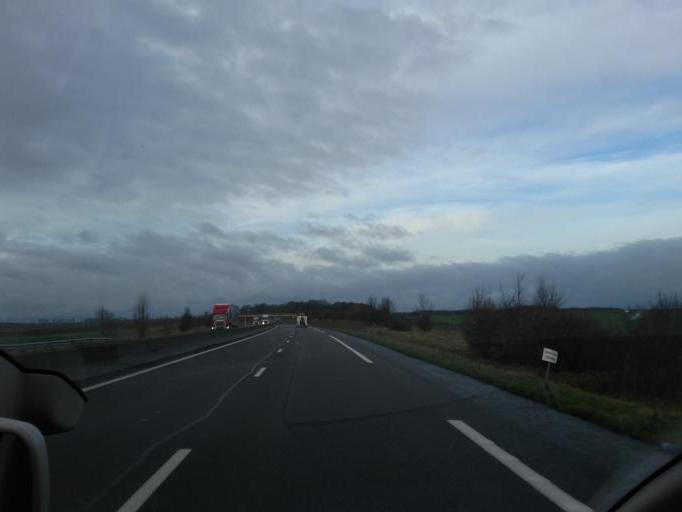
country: FR
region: Picardie
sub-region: Departement de la Somme
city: Harbonnieres
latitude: 49.8608
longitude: 2.6832
